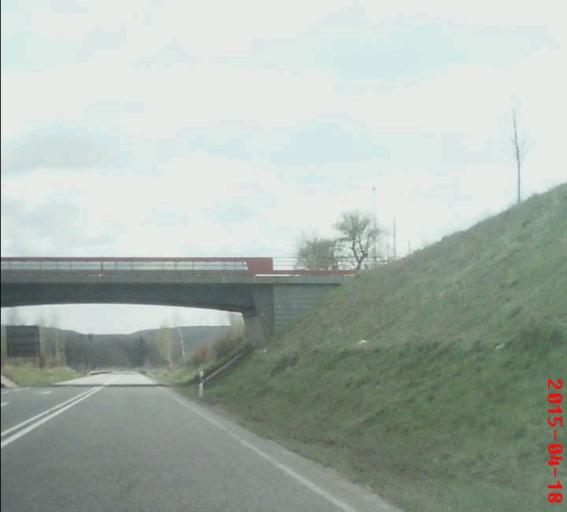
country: DE
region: Thuringia
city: Leinefelde
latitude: 51.3896
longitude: 10.3463
